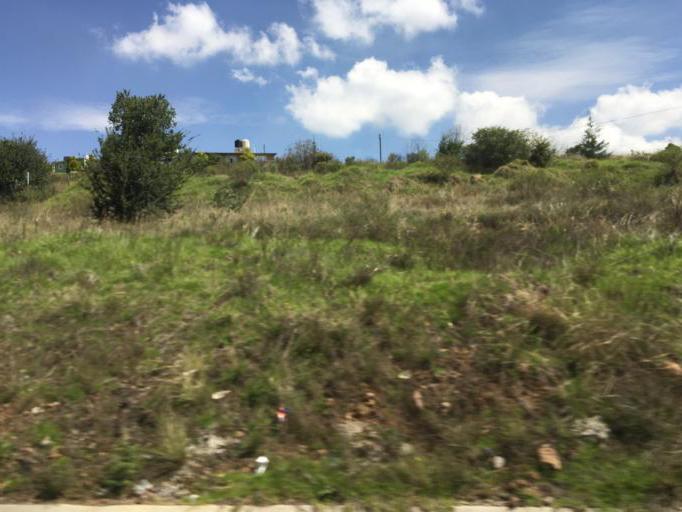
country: MX
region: Mexico
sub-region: Timilpan
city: Tercera Manzana de Zaragoza
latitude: 19.8831
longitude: -99.6574
